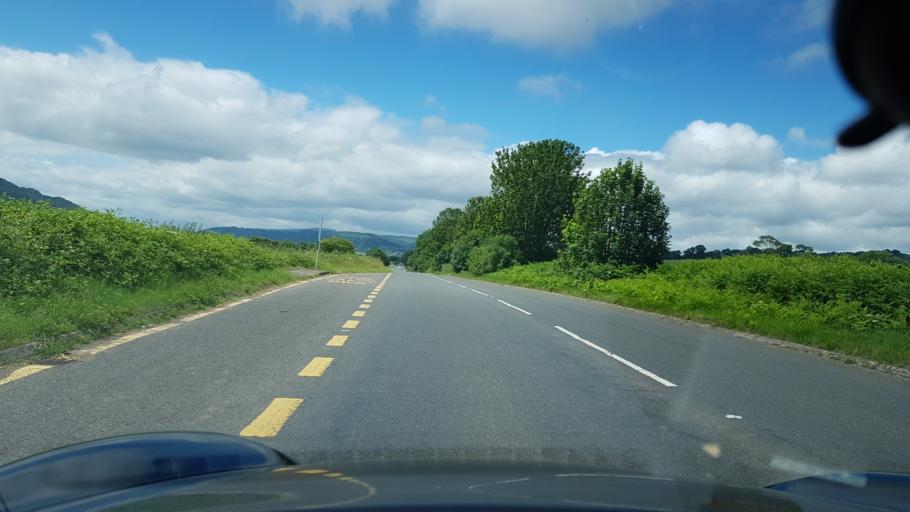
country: GB
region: Wales
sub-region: Monmouthshire
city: Abergavenny
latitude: 51.7953
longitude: -2.9932
